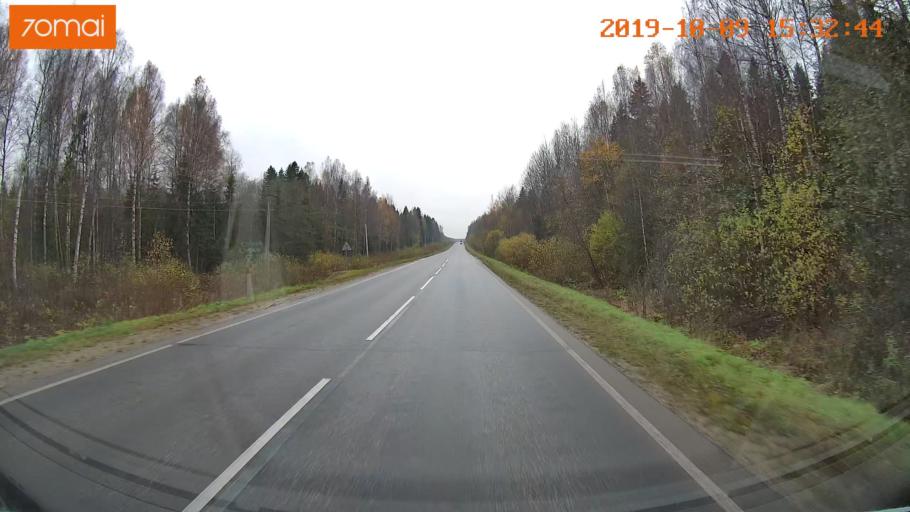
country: RU
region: Kostroma
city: Oktyabr'skiy
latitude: 57.9613
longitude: 41.2719
